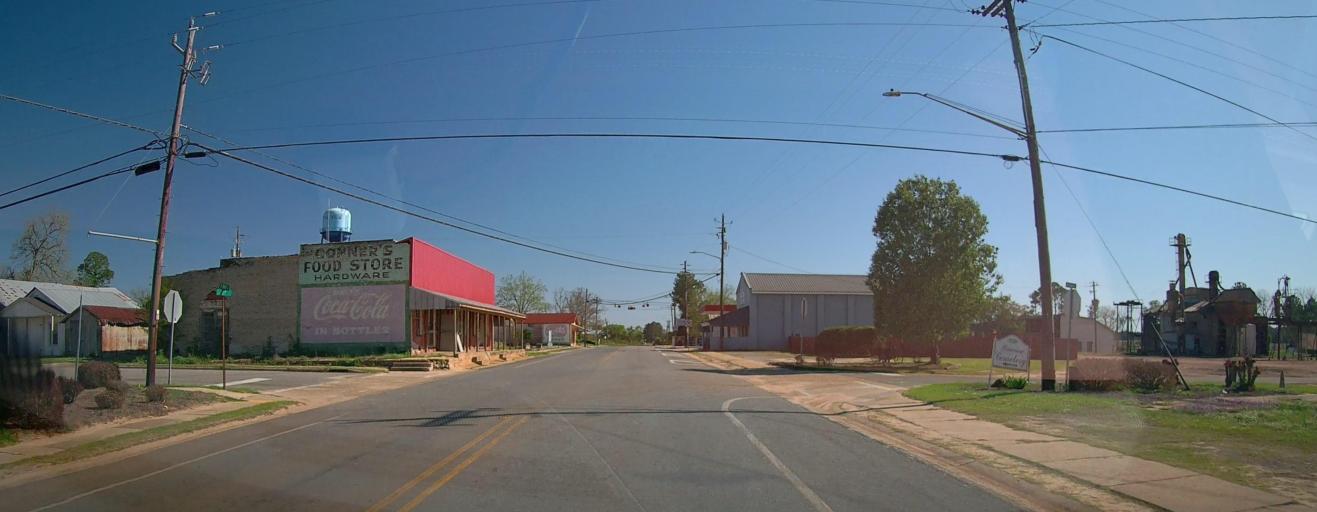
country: US
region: Georgia
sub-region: Wilcox County
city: Rochelle
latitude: 32.1112
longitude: -83.5011
